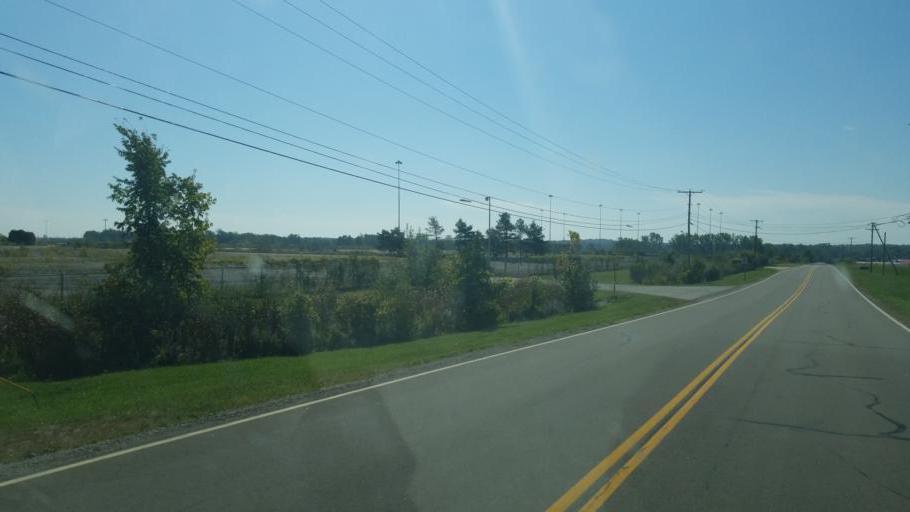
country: US
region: Ohio
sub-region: Richland County
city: Ontario
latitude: 40.7742
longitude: -82.6100
